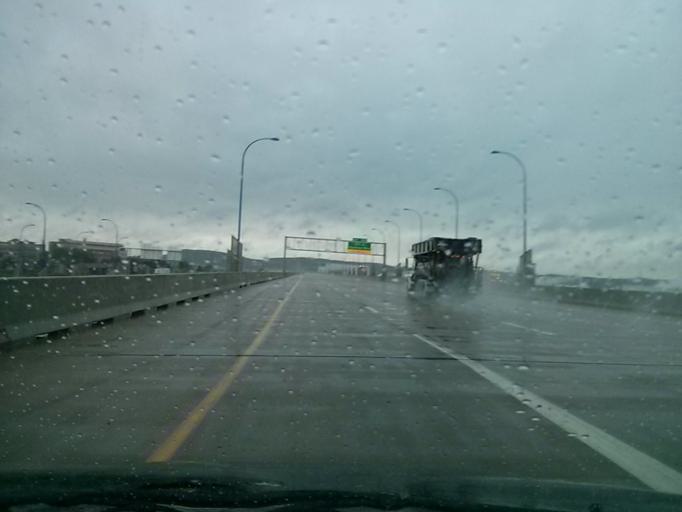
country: US
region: Oklahoma
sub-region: Tulsa County
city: Tulsa
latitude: 36.1452
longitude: -96.0041
